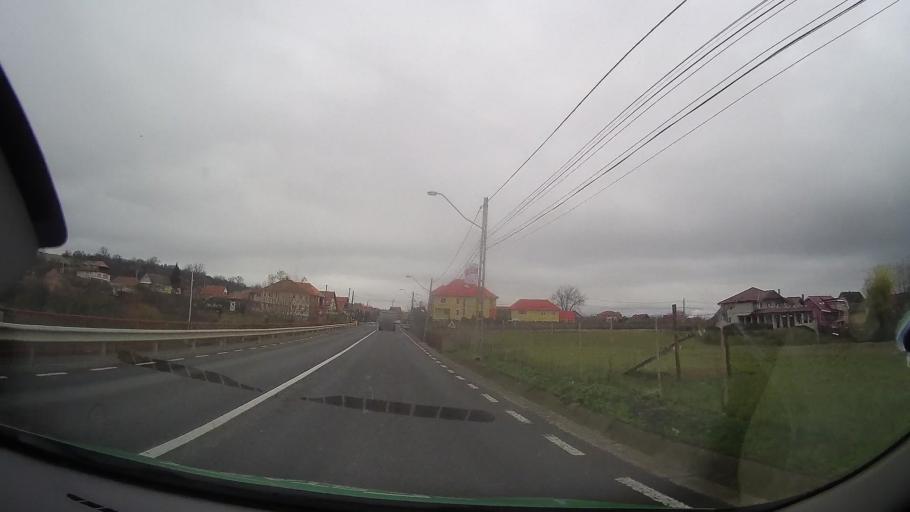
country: RO
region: Mures
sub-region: Municipiul Reghin
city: Reghin
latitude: 46.7701
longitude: 24.6855
